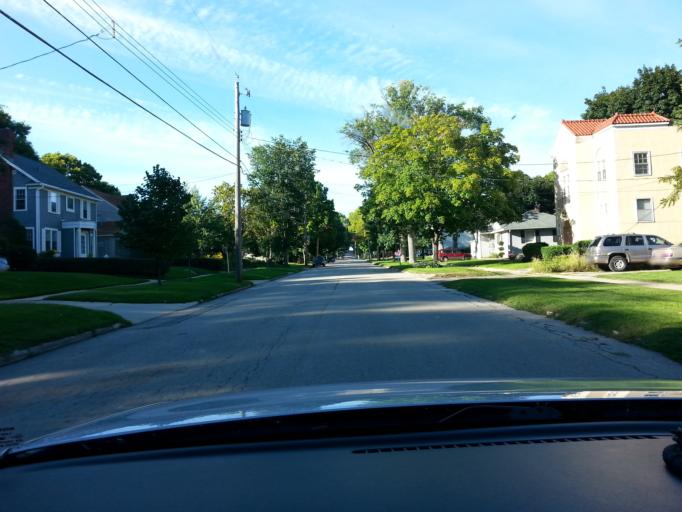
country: US
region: Minnesota
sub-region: Olmsted County
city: Rochester
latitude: 44.0149
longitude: -92.4730
